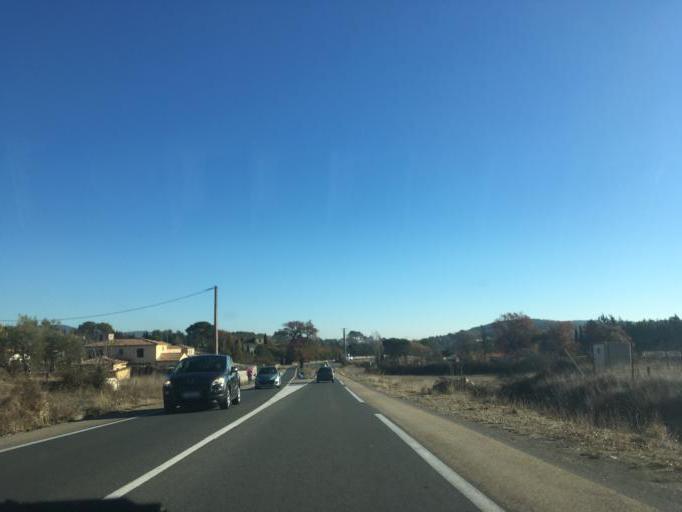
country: FR
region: Provence-Alpes-Cote d'Azur
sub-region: Departement du Var
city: Flayosc
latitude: 43.5289
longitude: 6.4248
